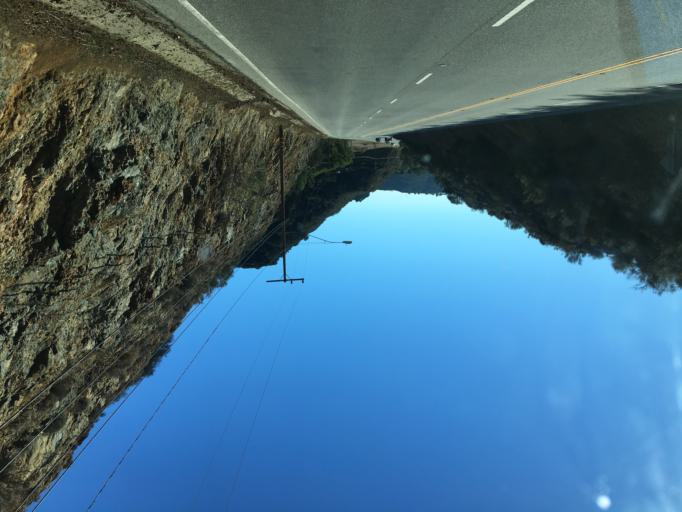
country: US
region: California
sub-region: Los Angeles County
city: Malibu
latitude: 34.0684
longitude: -118.8114
